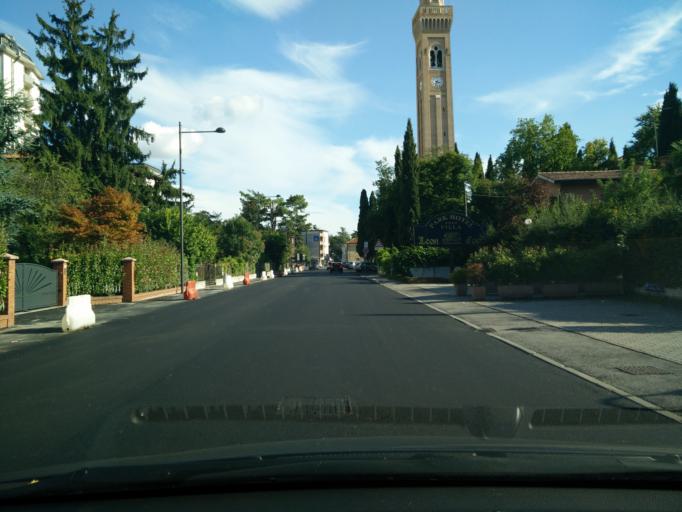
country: IT
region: Veneto
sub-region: Provincia di Venezia
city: Noventa di Piave
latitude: 45.6630
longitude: 12.5282
